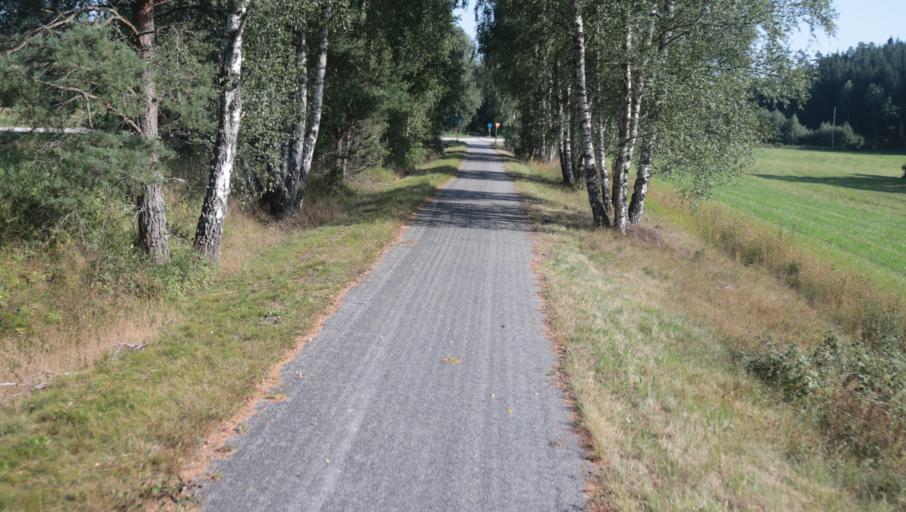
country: SE
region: Blekinge
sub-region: Karlshamns Kommun
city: Svangsta
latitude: 56.2989
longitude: 14.7347
